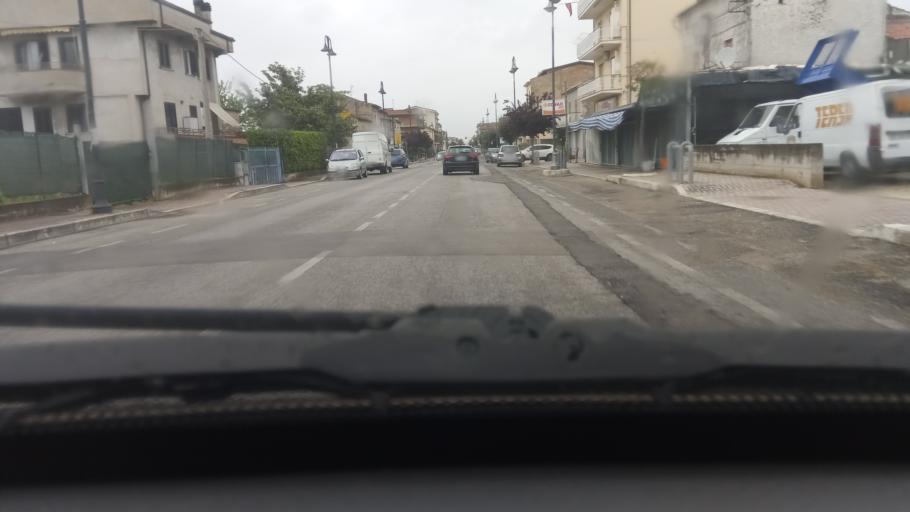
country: IT
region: Latium
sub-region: Provincia di Latina
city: Minturno
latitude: 41.2479
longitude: 13.7448
